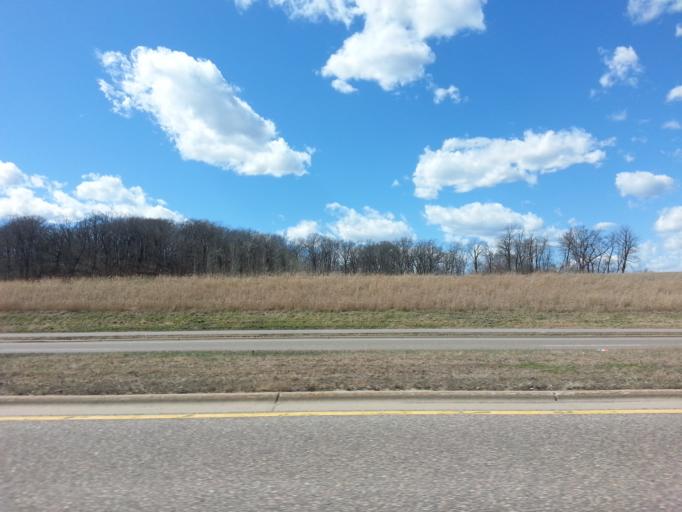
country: US
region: Minnesota
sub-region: Scott County
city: Prior Lake
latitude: 44.7230
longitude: -93.3753
